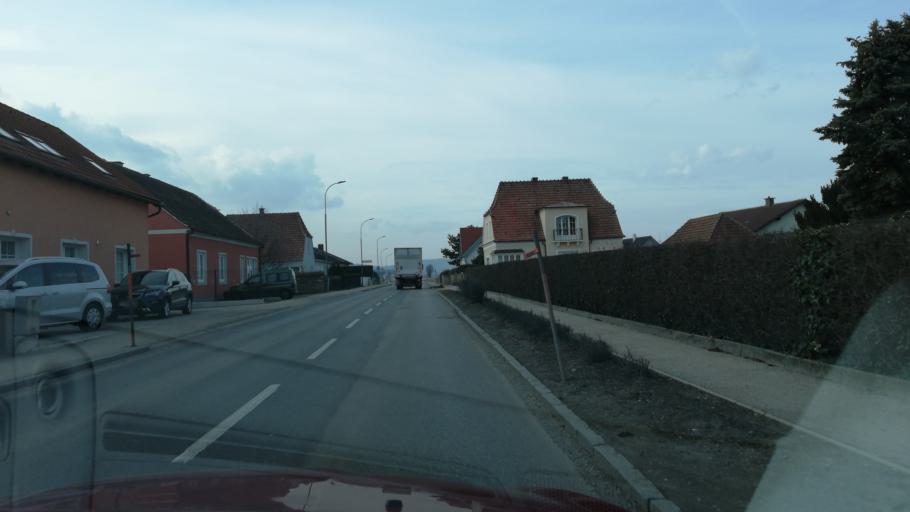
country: AT
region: Lower Austria
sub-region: Politischer Bezirk Tulln
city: Grafenworth
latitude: 48.3372
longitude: 15.8033
